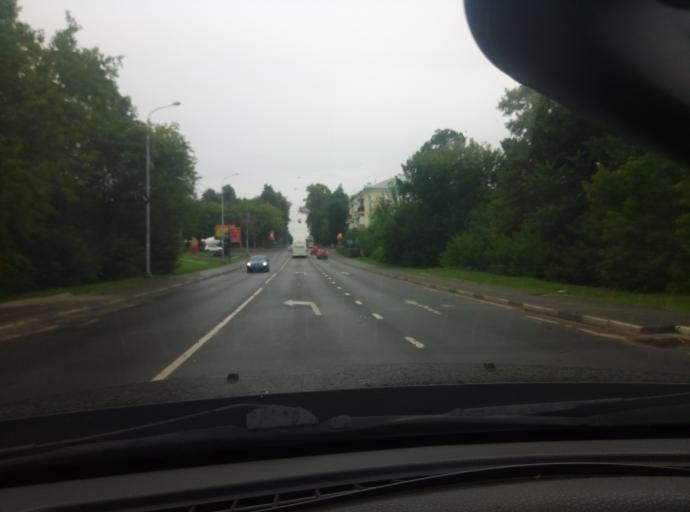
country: RU
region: Moskovskaya
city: Serpukhov
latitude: 54.9192
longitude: 37.4095
